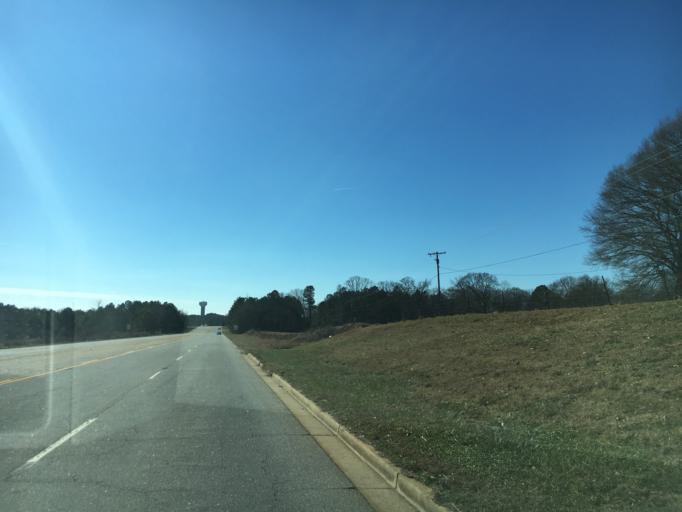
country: US
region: South Carolina
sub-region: Anderson County
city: Homeland Park
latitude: 34.4216
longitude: -82.6713
